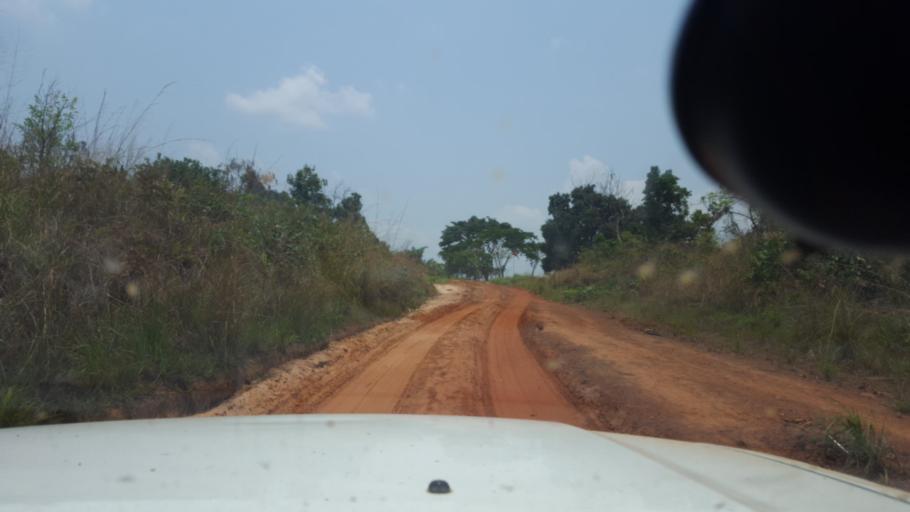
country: CD
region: Bandundu
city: Mushie
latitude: -3.7514
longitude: 16.6282
